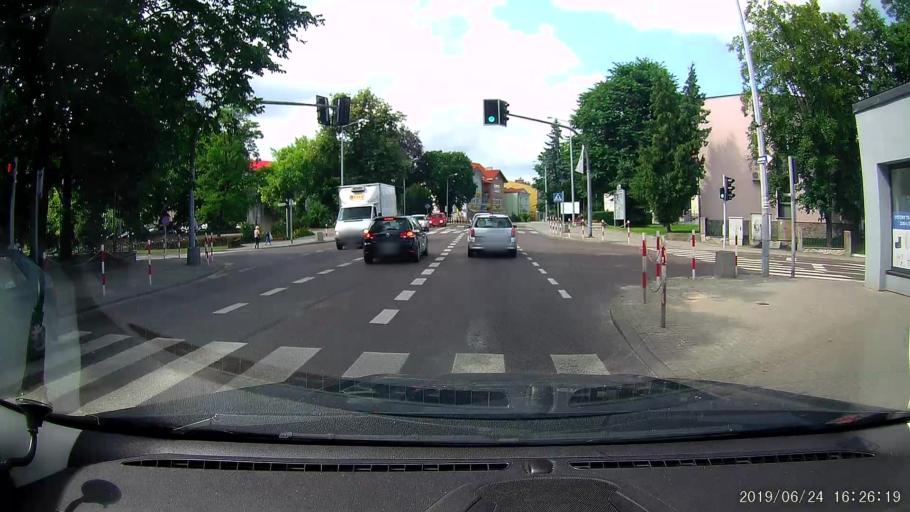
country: PL
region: Lublin Voivodeship
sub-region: Powiat tomaszowski
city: Tomaszow Lubelski
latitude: 50.4464
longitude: 23.4165
